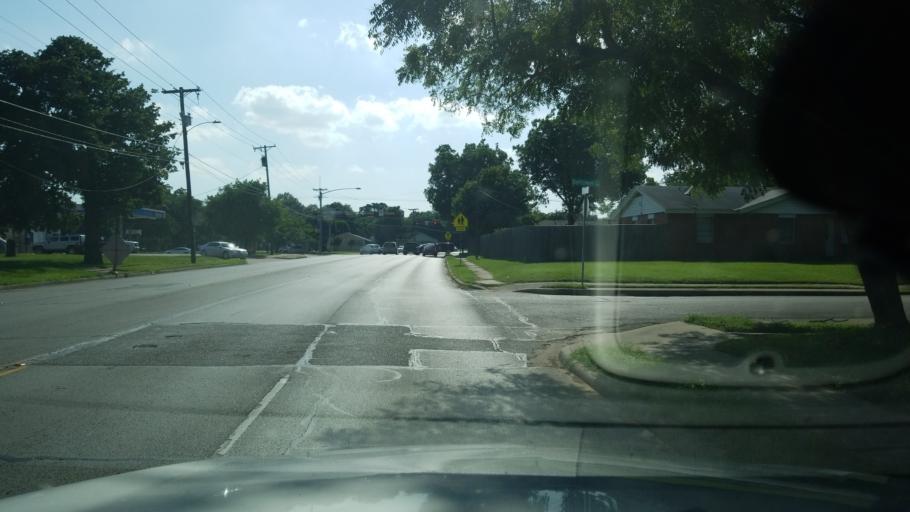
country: US
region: Texas
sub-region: Dallas County
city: Irving
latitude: 32.8225
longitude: -96.9752
